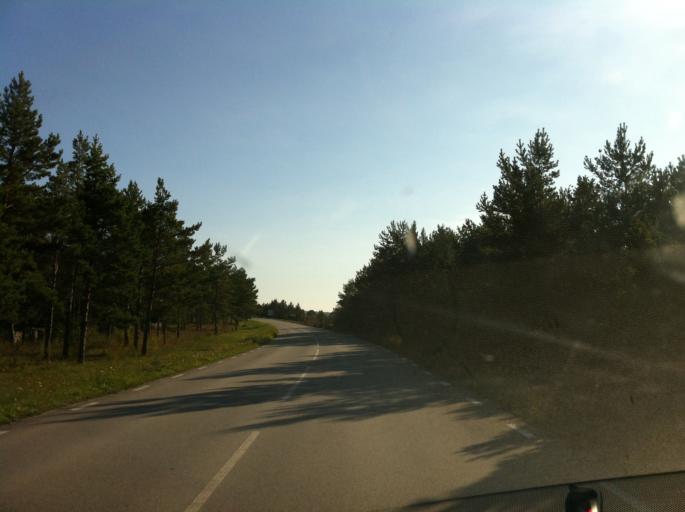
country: SE
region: Gotland
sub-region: Gotland
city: Slite
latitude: 57.8754
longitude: 19.0852
